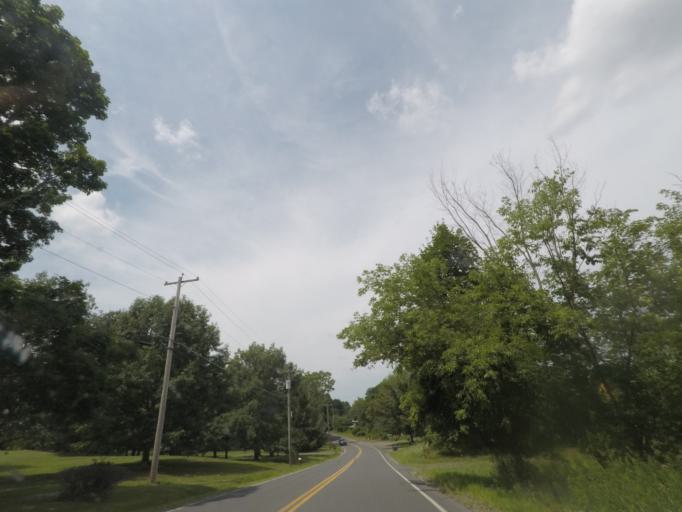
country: US
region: New York
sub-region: Rensselaer County
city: Wynantskill
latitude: 42.7161
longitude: -73.6483
